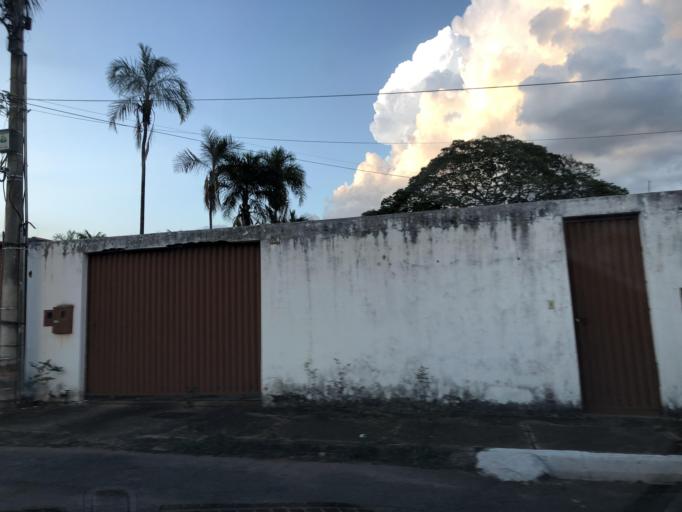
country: BR
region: Federal District
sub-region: Brasilia
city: Brasilia
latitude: -15.8472
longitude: -47.8944
